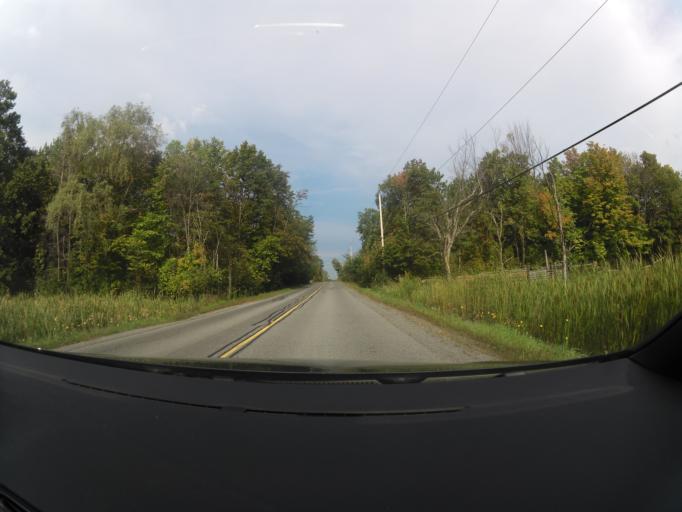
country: CA
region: Ontario
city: Bells Corners
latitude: 45.3942
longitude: -76.0104
